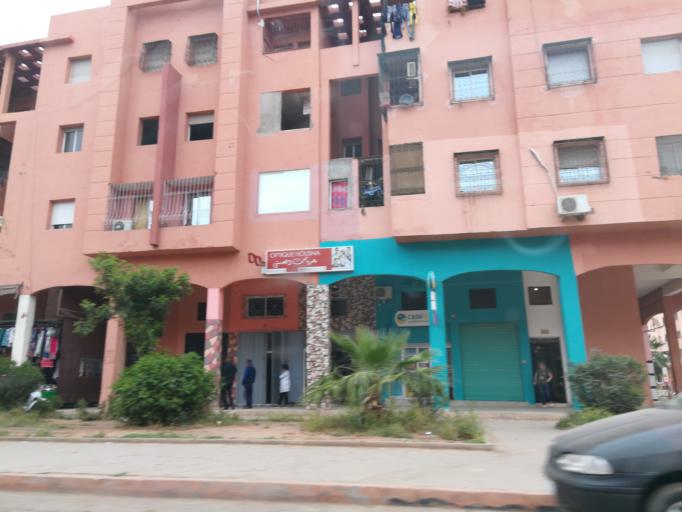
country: MA
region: Marrakech-Tensift-Al Haouz
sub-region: Marrakech
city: Marrakesh
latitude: 31.5755
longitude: -8.0586
